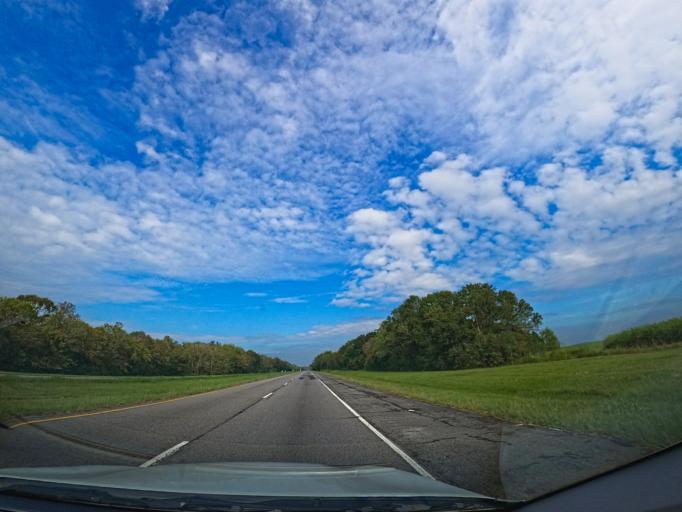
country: US
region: Louisiana
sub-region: Saint Mary Parish
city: Patterson
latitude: 29.7086
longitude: -91.3914
